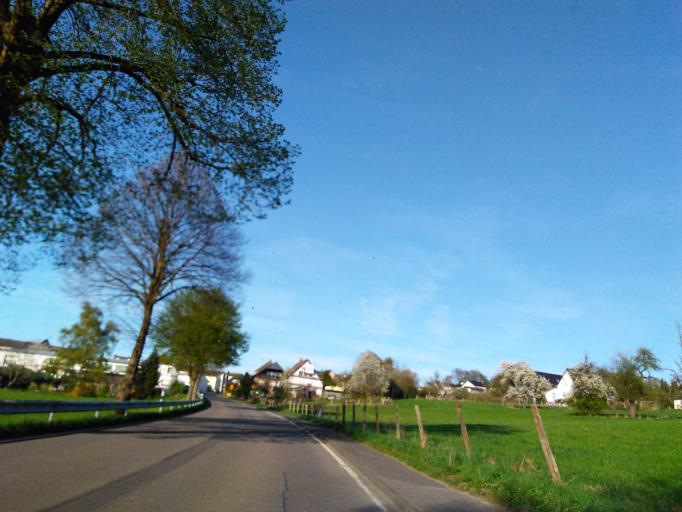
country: DE
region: North Rhine-Westphalia
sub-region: Regierungsbezirk Koln
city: Much
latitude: 50.9429
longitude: 7.4480
